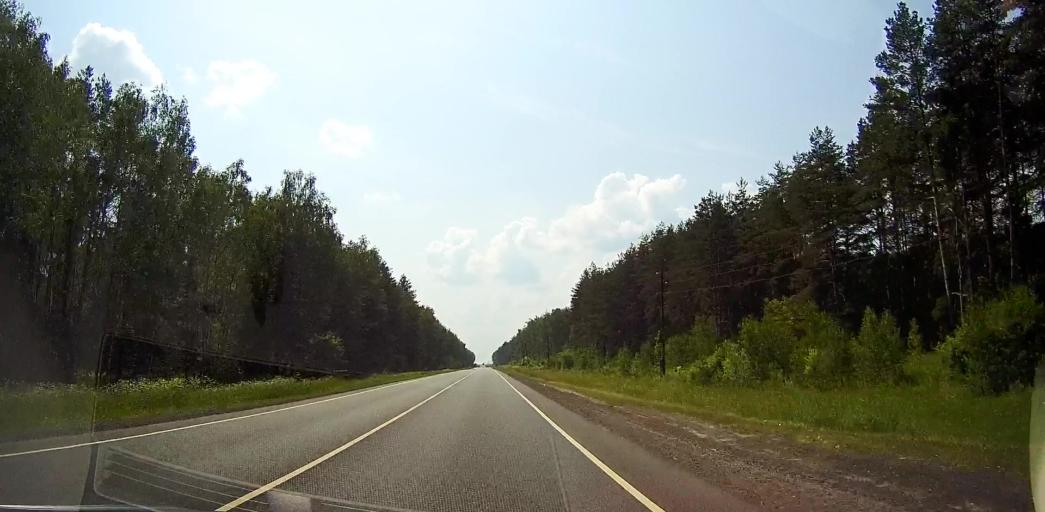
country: RU
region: Moskovskaya
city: Meshcherino
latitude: 55.1672
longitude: 38.3234
